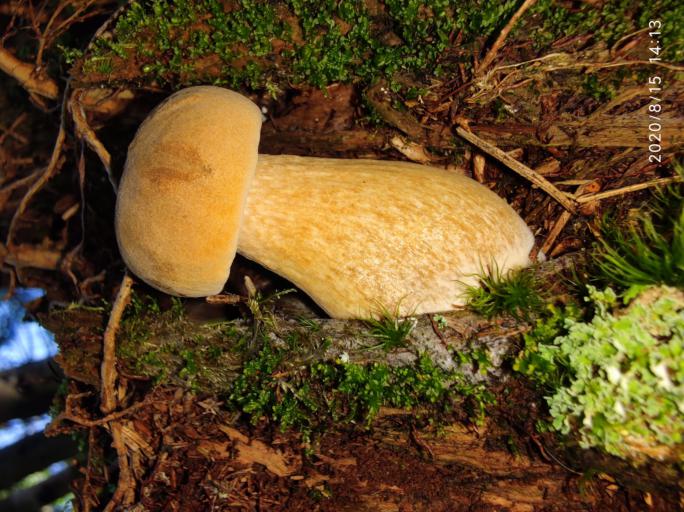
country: NO
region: Akershus
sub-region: Nittedal
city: Rotnes
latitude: 60.0624
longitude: 10.8491
